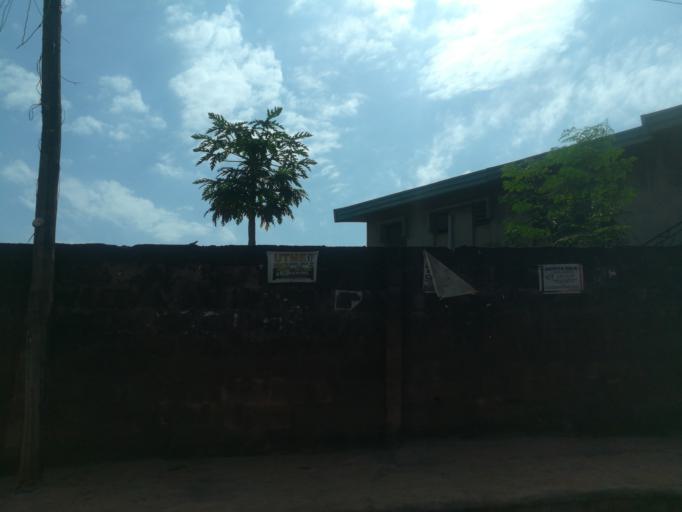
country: NG
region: Oyo
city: Ibadan
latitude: 7.4193
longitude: 3.9761
